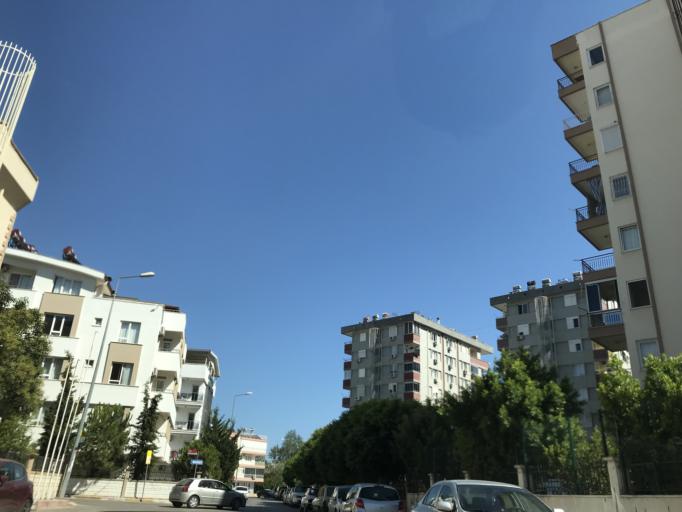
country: TR
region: Antalya
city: Antalya
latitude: 36.9018
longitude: 30.6577
